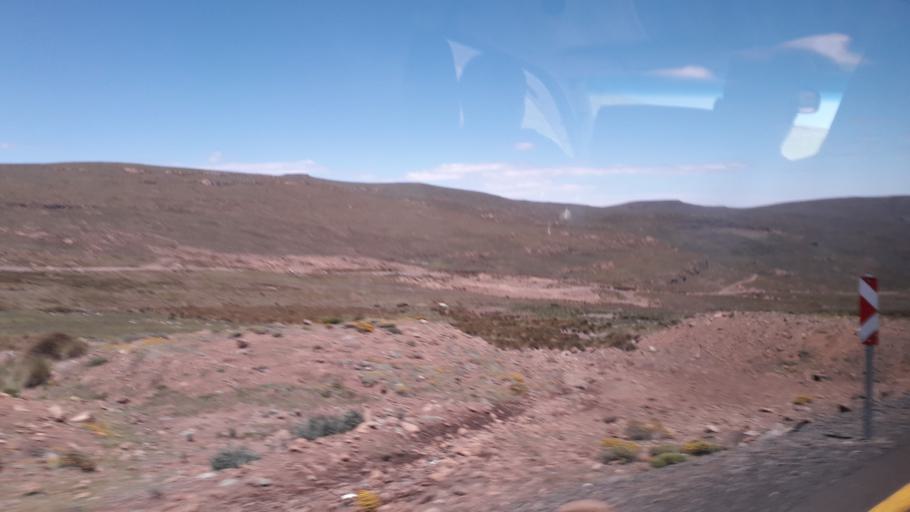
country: ZA
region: Orange Free State
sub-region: Thabo Mofutsanyana District Municipality
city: Phuthaditjhaba
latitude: -28.8129
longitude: 28.7151
